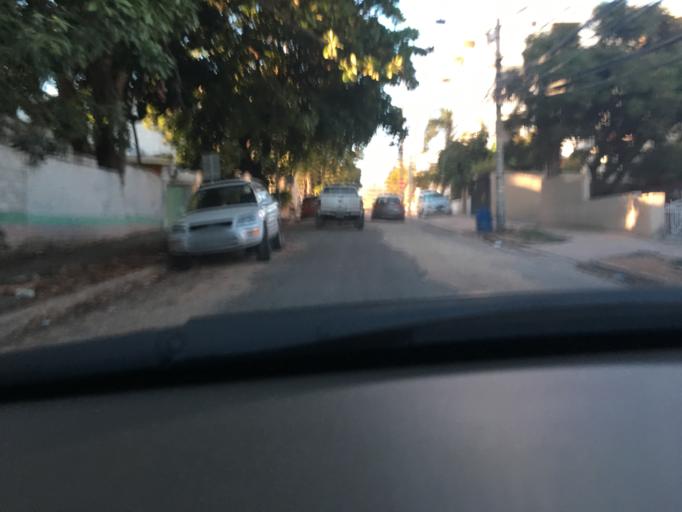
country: DO
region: Nacional
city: Ciudad Nueva
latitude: 18.4723
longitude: -69.8993
